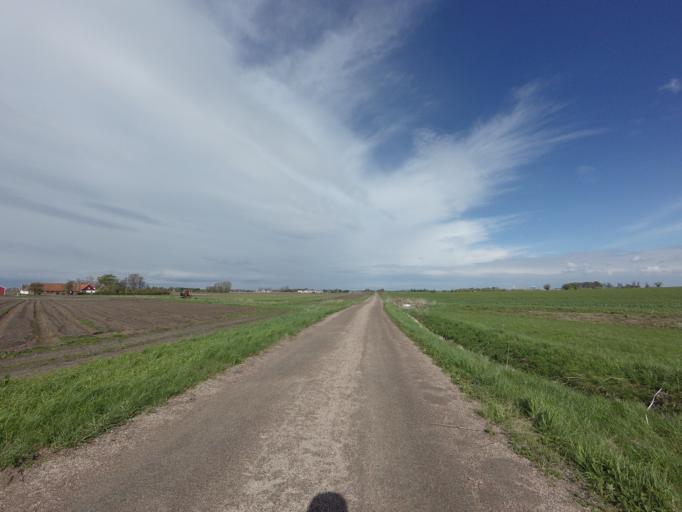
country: SE
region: Skane
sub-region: Malmo
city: Tygelsjo
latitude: 55.5313
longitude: 12.9806
